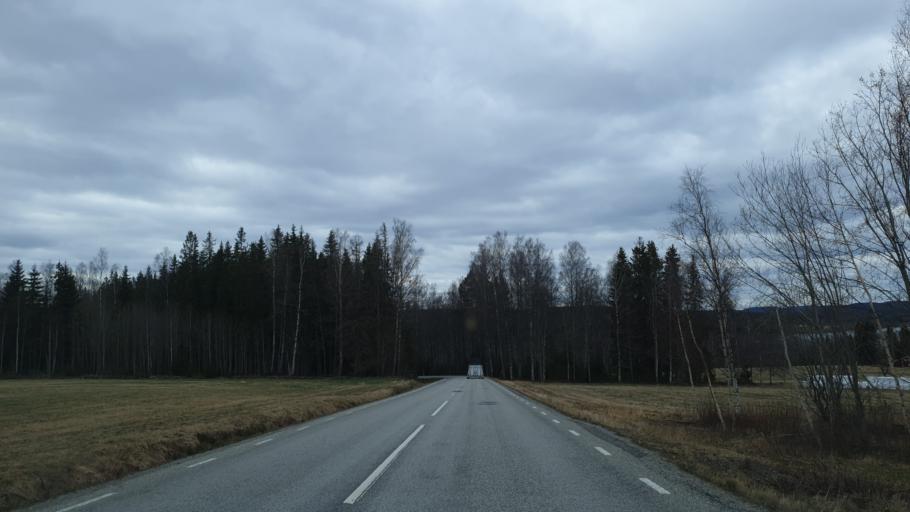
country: SE
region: OErebro
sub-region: Nora Kommun
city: As
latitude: 59.6001
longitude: 14.9358
